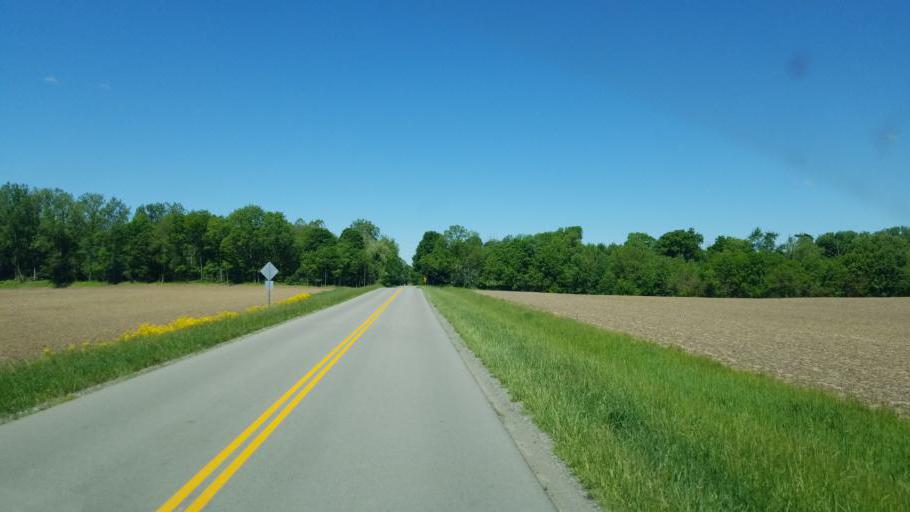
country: US
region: Ohio
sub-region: Logan County
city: Russells Point
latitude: 40.4205
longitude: -83.9137
